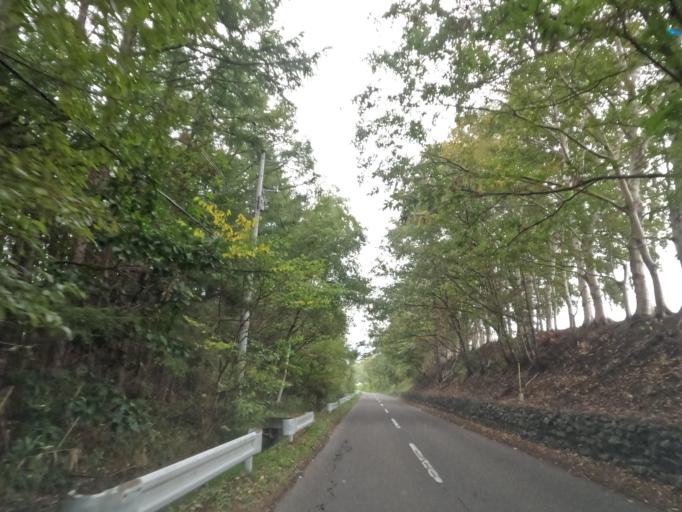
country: JP
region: Hokkaido
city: Date
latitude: 42.4745
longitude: 140.8903
